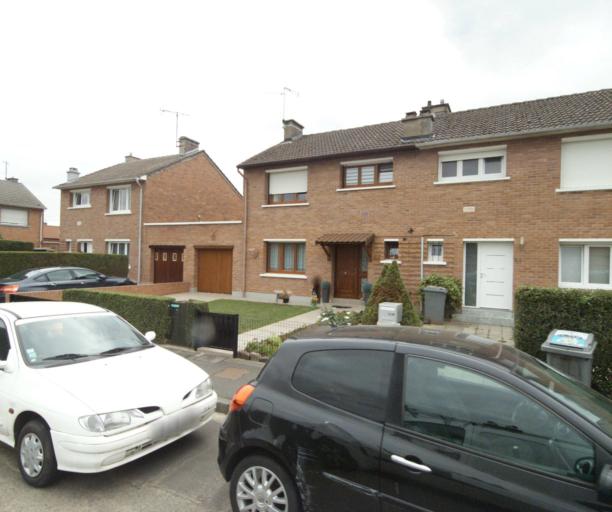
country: FR
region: Nord-Pas-de-Calais
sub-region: Departement du Nord
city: Sainghin-en-Melantois
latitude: 50.5688
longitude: 3.1659
